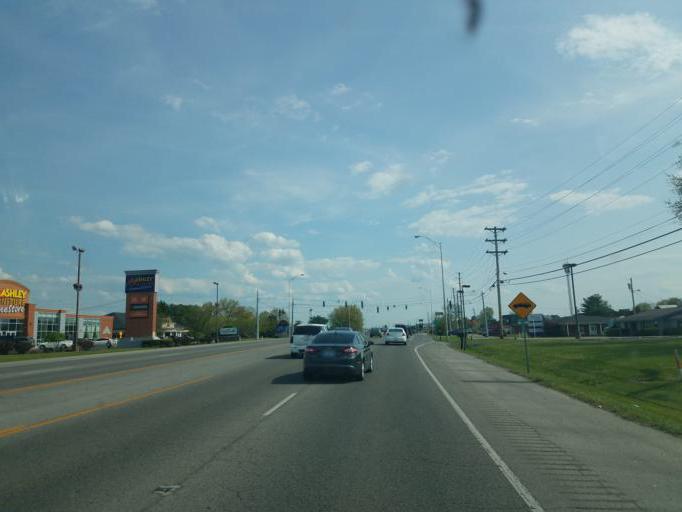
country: US
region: Kentucky
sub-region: Warren County
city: Bowling Green
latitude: 36.9651
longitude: -86.4318
